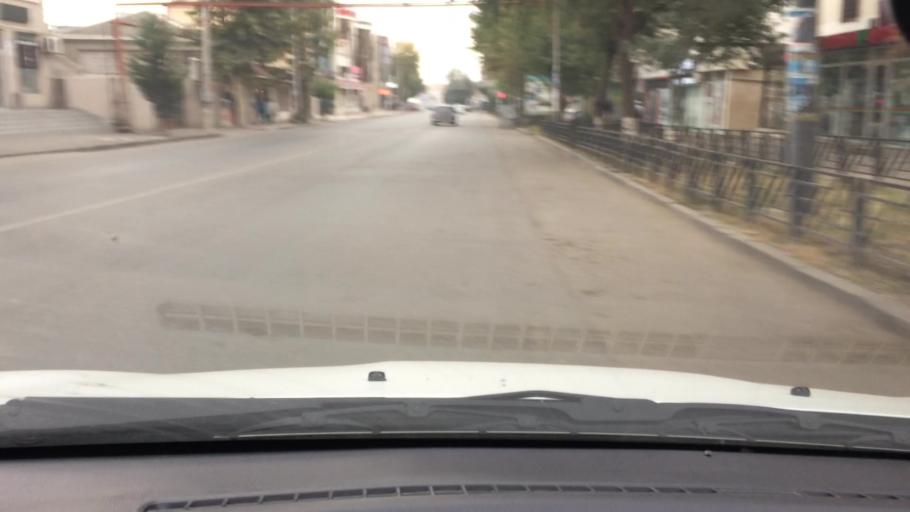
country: GE
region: Kvemo Kartli
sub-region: Marneuli
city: Marneuli
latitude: 41.4869
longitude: 44.7998
